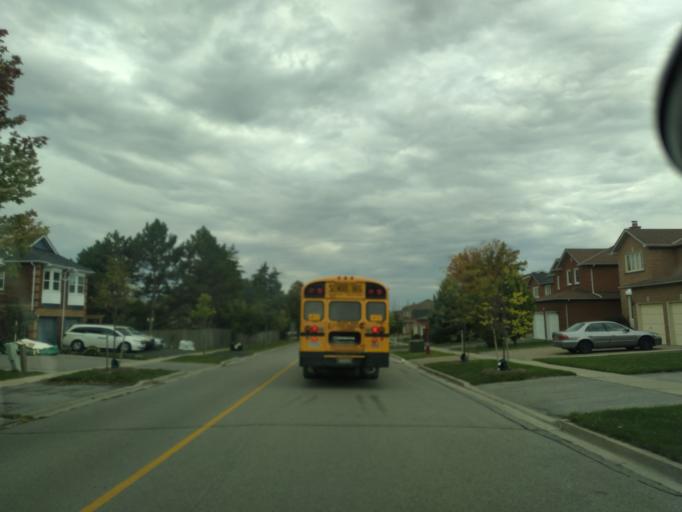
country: CA
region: Ontario
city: Newmarket
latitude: 44.0283
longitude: -79.4725
